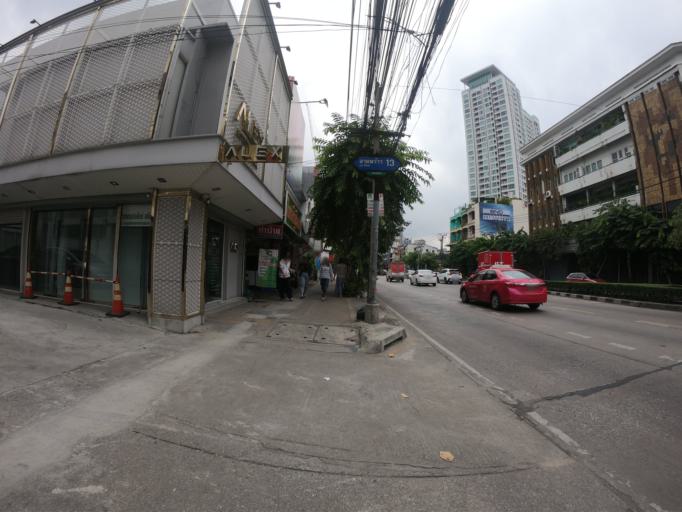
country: TH
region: Bangkok
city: Chatuchak
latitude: 13.8085
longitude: 100.5693
